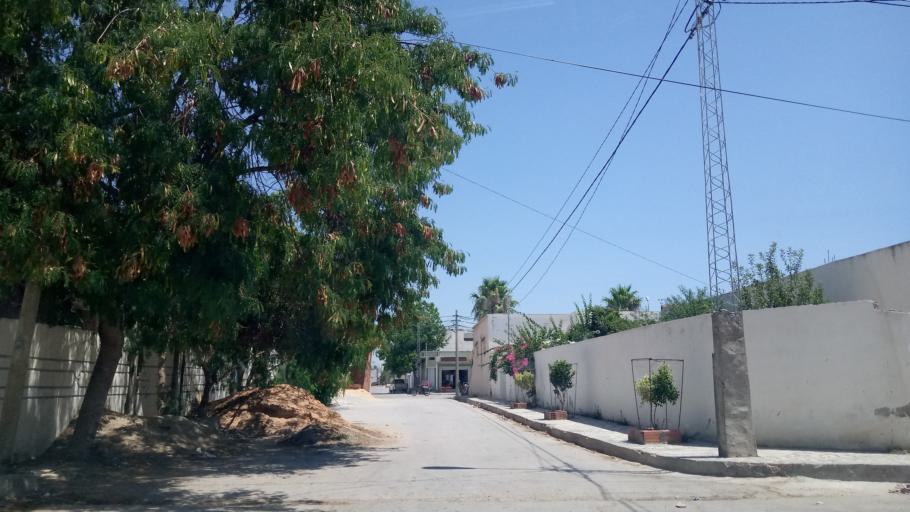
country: TN
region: Al Qayrawan
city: Sbikha
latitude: 36.1188
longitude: 10.0910
